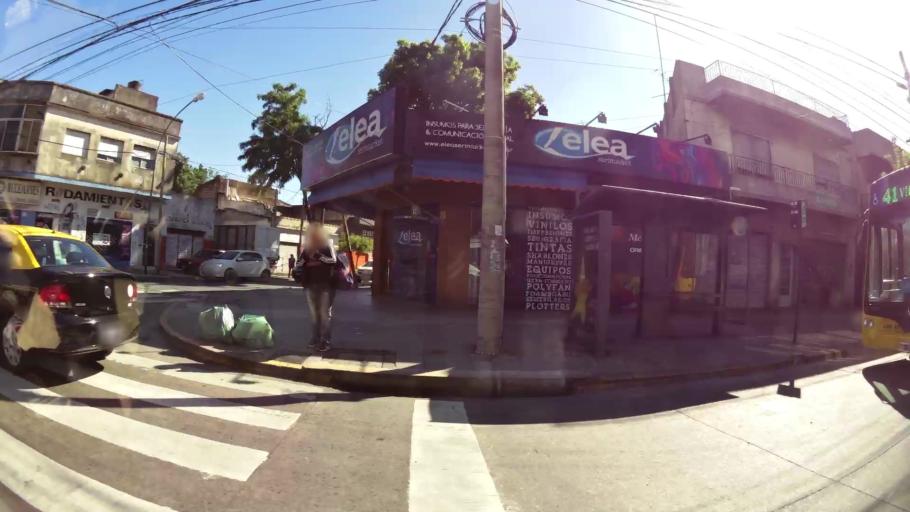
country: AR
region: Buenos Aires
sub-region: Partido de General San Martin
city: General San Martin
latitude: -34.5440
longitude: -58.5032
